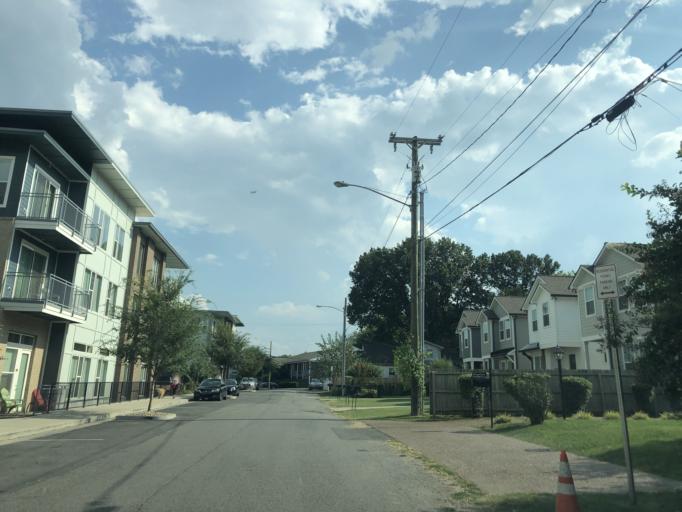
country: US
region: Tennessee
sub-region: Davidson County
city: Oak Hill
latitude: 36.1256
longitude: -86.7789
